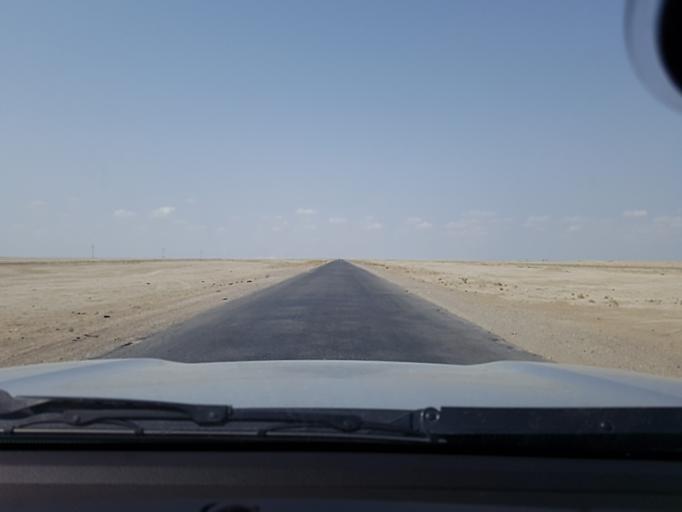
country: TM
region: Balkan
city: Gumdag
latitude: 38.6657
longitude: 54.4005
